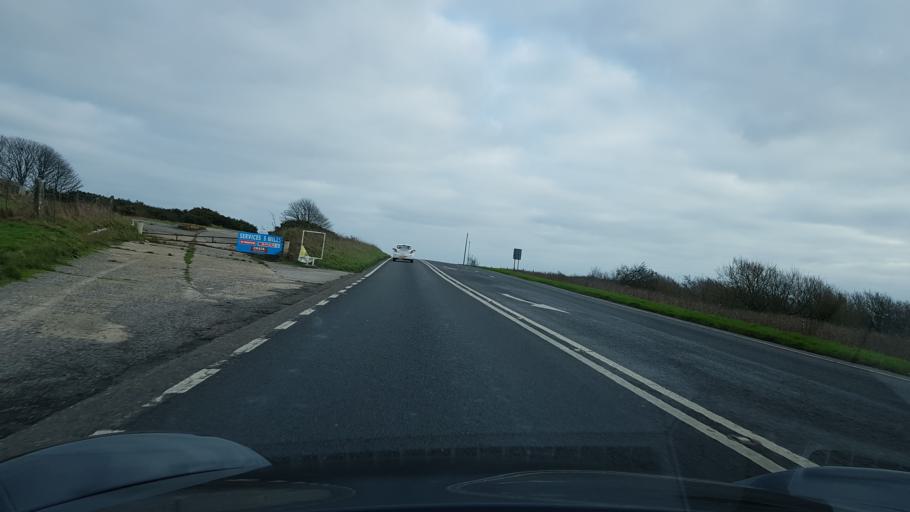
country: GB
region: England
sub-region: Dorset
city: Bridport
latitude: 50.7257
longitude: -2.6539
